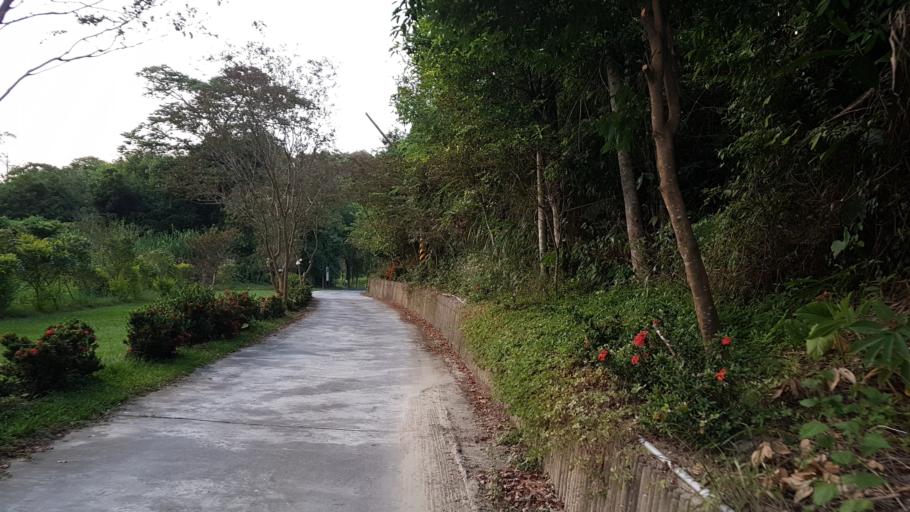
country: TW
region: Taiwan
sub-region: Chiayi
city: Jiayi Shi
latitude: 23.3614
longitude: 120.4684
